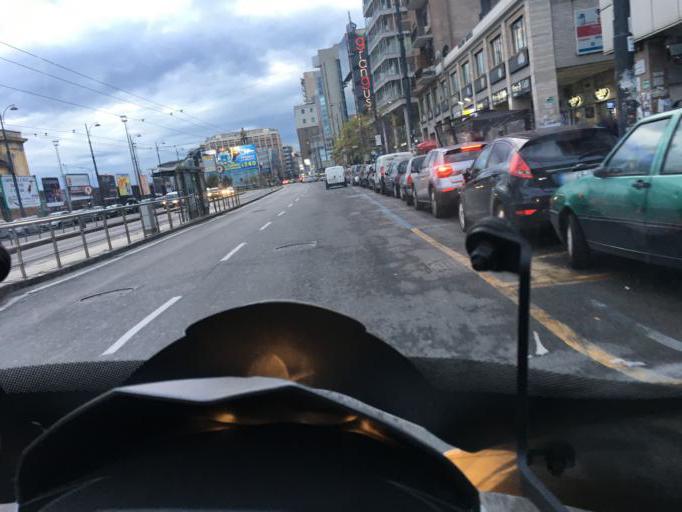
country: IT
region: Campania
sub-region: Provincia di Napoli
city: Napoli
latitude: 40.8447
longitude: 14.2597
